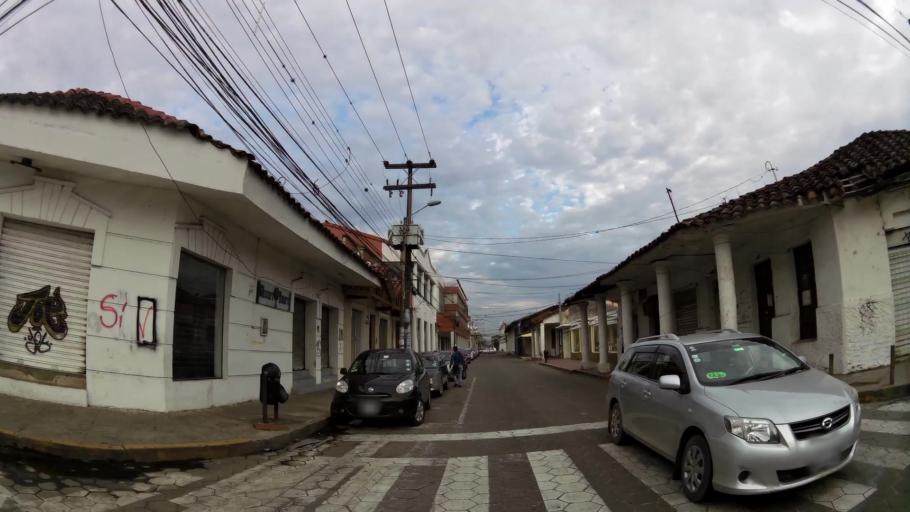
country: BO
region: Santa Cruz
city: Santa Cruz de la Sierra
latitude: -17.7816
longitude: -63.1797
